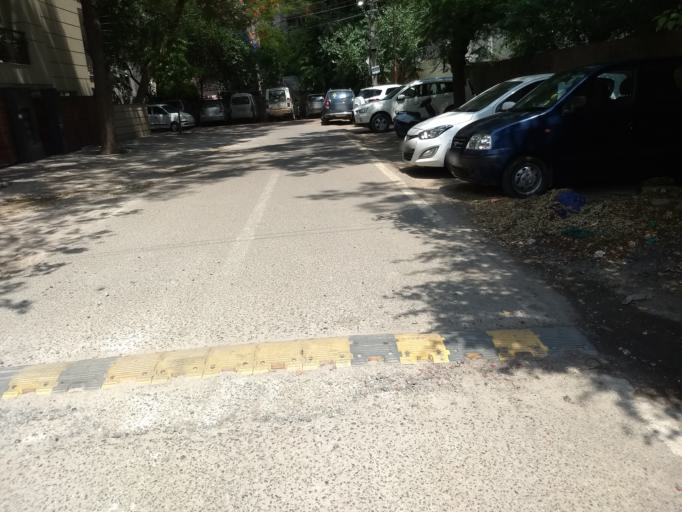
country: IN
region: NCT
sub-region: New Delhi
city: New Delhi
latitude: 28.5404
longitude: 77.2088
